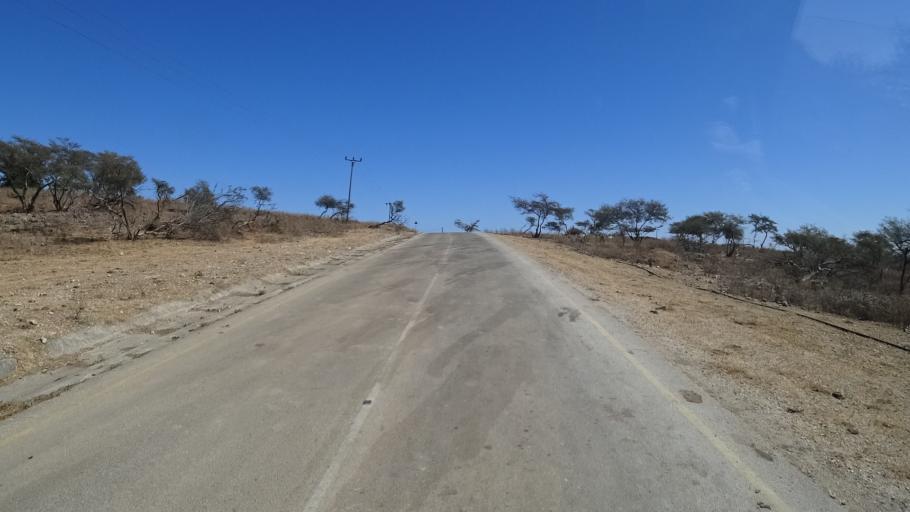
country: YE
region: Al Mahrah
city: Hawf
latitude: 16.7796
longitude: 53.3330
